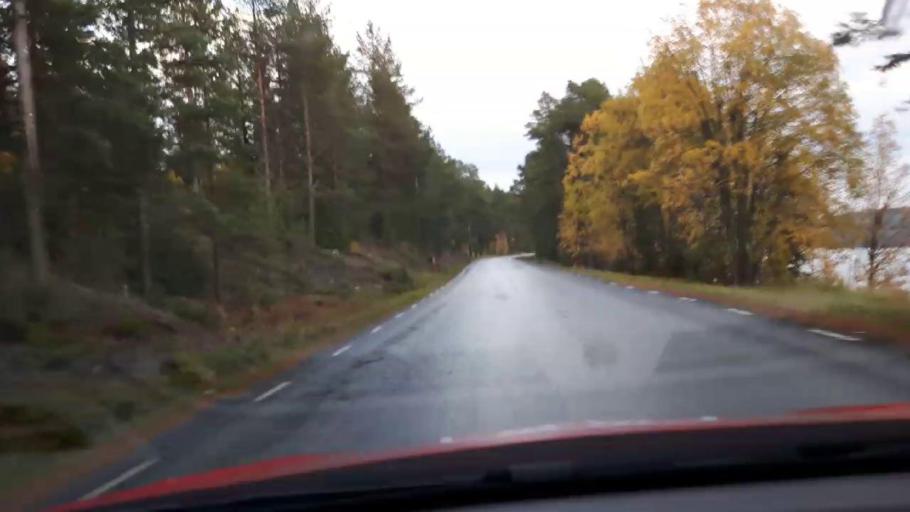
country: SE
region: Jaemtland
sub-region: OEstersunds Kommun
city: Lit
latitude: 63.3231
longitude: 14.9093
